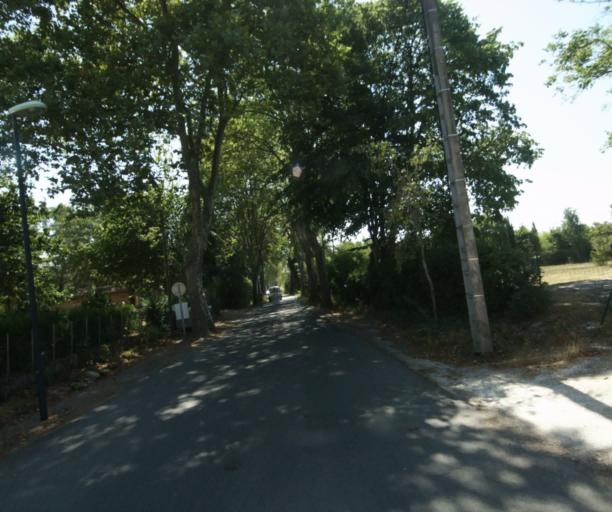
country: FR
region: Midi-Pyrenees
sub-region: Departement de la Haute-Garonne
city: Revel
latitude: 43.5035
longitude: 1.9490
